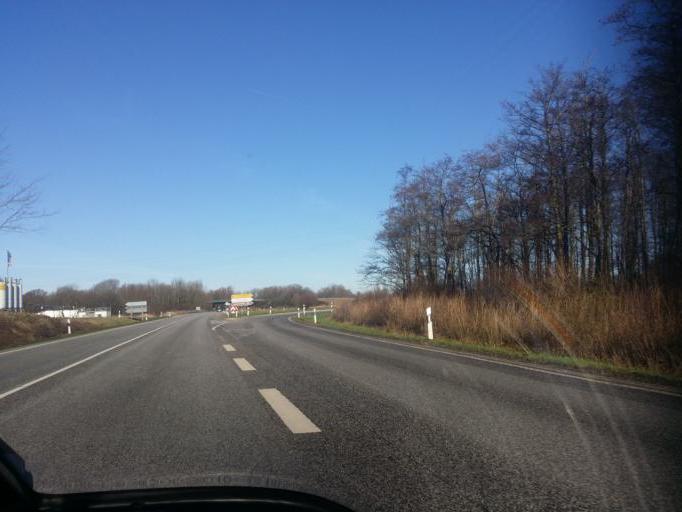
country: DE
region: Schleswig-Holstein
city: Tonning
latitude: 54.3257
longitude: 8.9544
